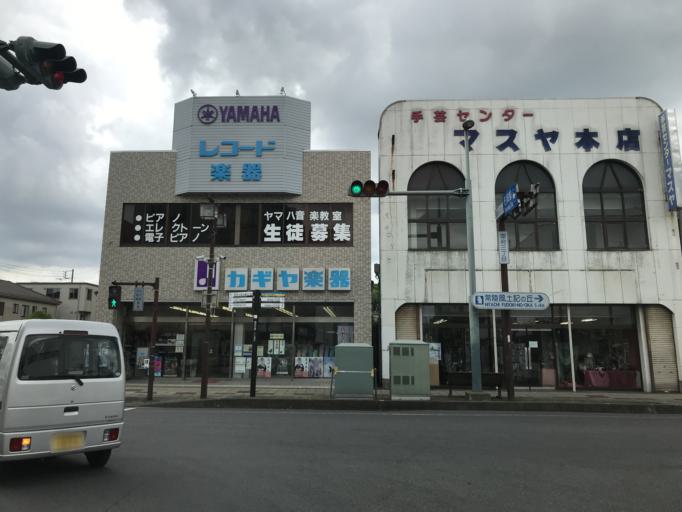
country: JP
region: Ibaraki
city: Ishioka
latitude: 36.1908
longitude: 140.2743
